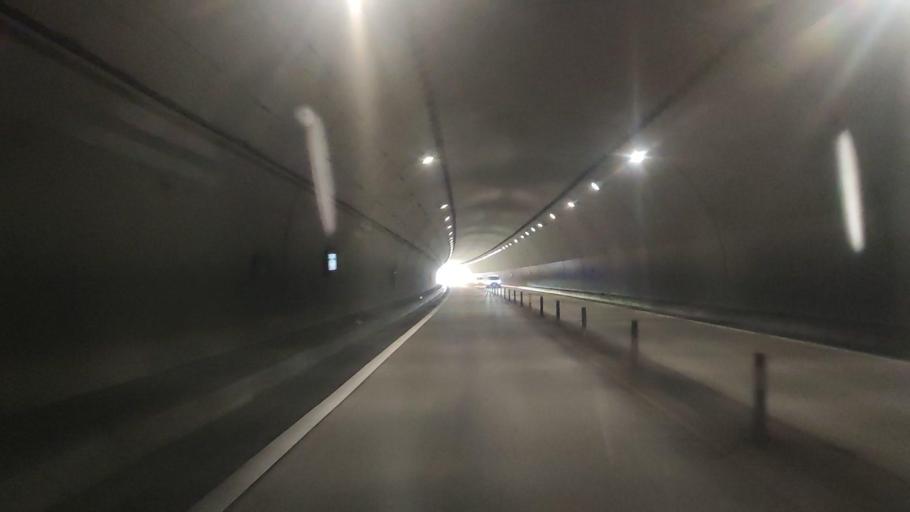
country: JP
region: Nagasaki
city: Shimabara
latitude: 32.7729
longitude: 130.3570
